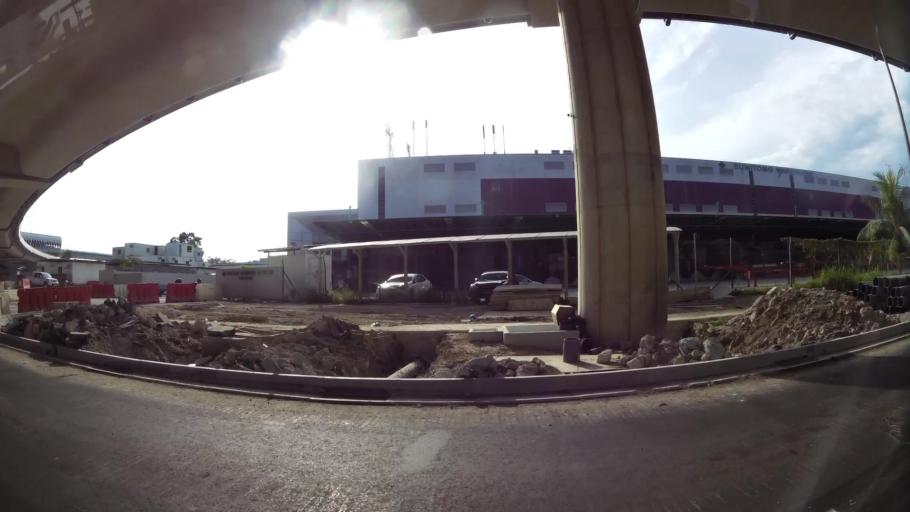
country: MY
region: Johor
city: Johor Bahru
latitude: 1.3289
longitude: 103.6373
